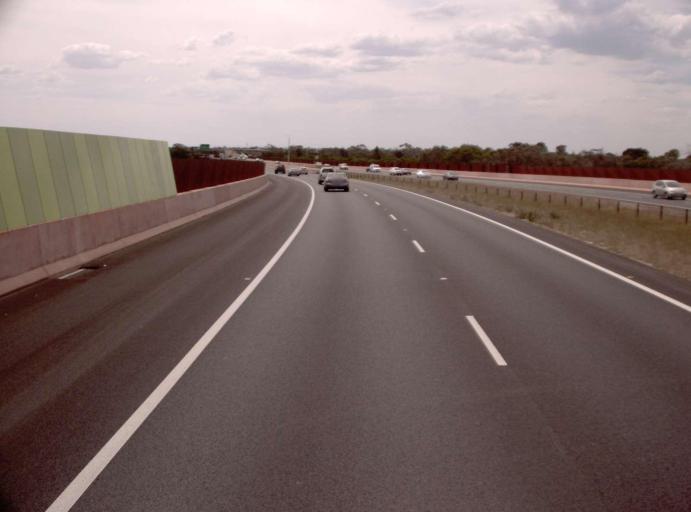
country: AU
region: Victoria
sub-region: Frankston
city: Carrum Downs
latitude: -38.1200
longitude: 145.1710
